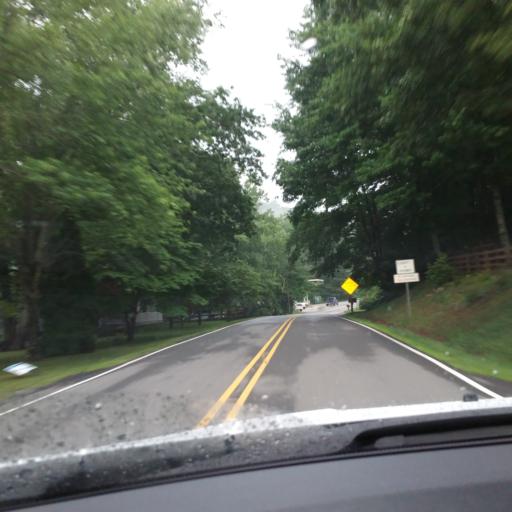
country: US
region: North Carolina
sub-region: Yancey County
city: Burnsville
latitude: 35.8090
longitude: -82.1992
